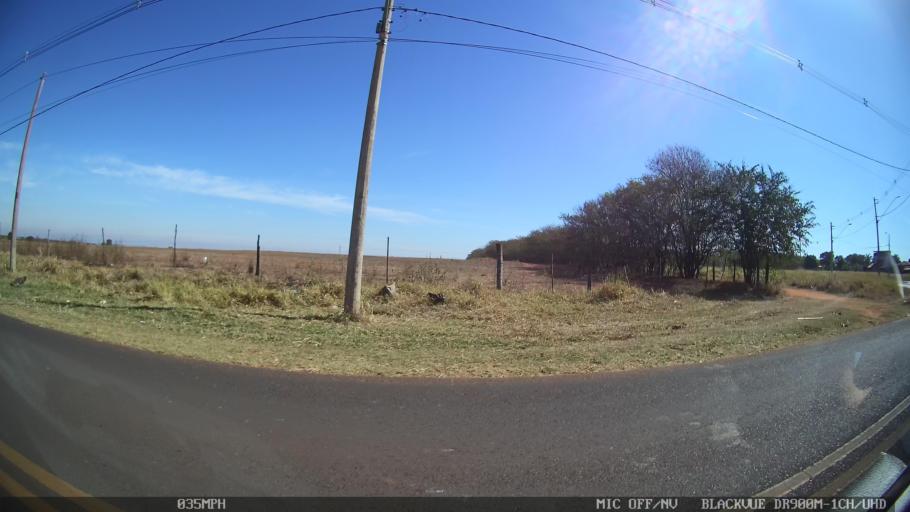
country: BR
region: Sao Paulo
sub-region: Sao Jose Do Rio Preto
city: Sao Jose do Rio Preto
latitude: -20.7412
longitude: -49.4342
